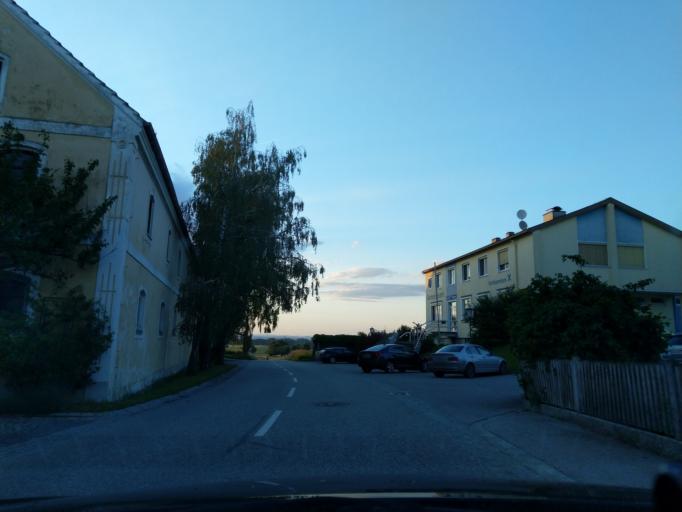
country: DE
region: Bavaria
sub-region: Lower Bavaria
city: Bad Fussing
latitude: 48.3042
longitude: 13.3656
